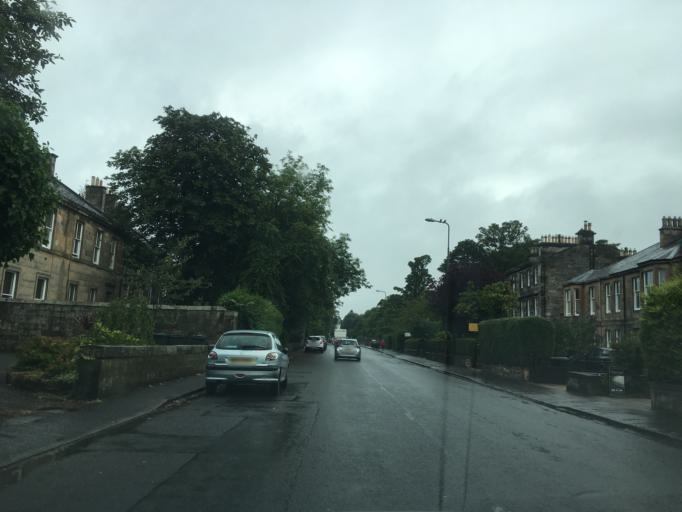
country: GB
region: Scotland
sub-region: Edinburgh
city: Edinburgh
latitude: 55.9737
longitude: -3.1901
